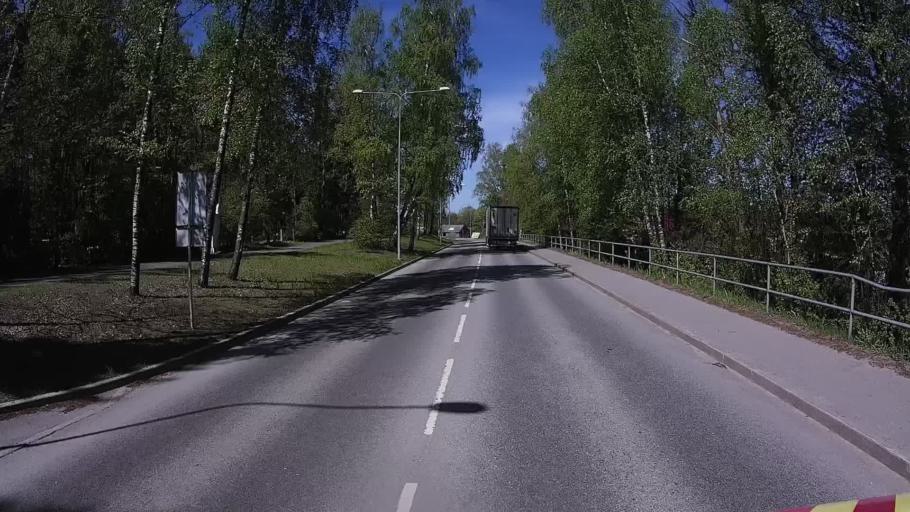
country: EE
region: Vorumaa
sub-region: Voru linn
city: Voru
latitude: 57.8251
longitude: 27.0156
